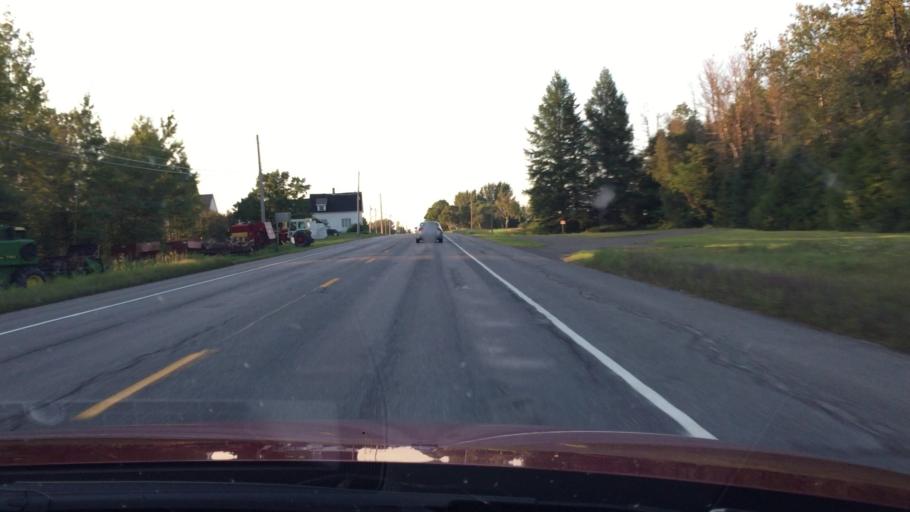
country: US
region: Maine
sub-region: Aroostook County
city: Houlton
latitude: 46.1762
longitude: -67.8409
